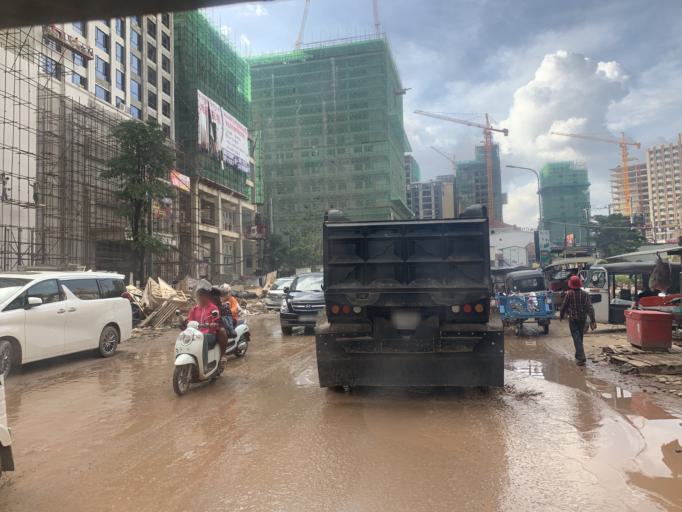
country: KH
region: Preah Sihanouk
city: Sihanoukville
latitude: 10.6085
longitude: 103.5243
